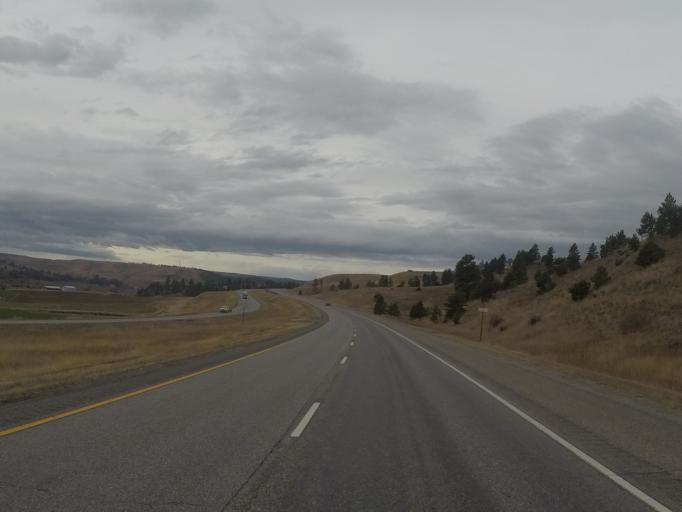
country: US
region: Montana
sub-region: Stillwater County
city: Columbus
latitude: 45.5985
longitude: -109.0748
